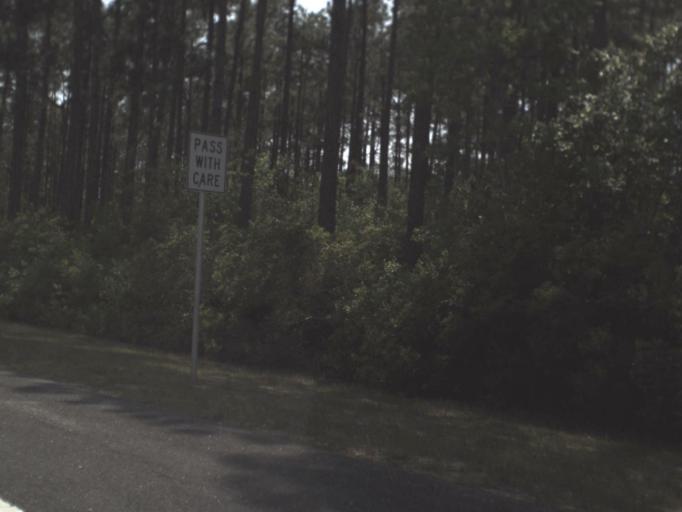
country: US
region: Florida
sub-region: Santa Rosa County
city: Bagdad
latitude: 30.4985
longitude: -87.0808
